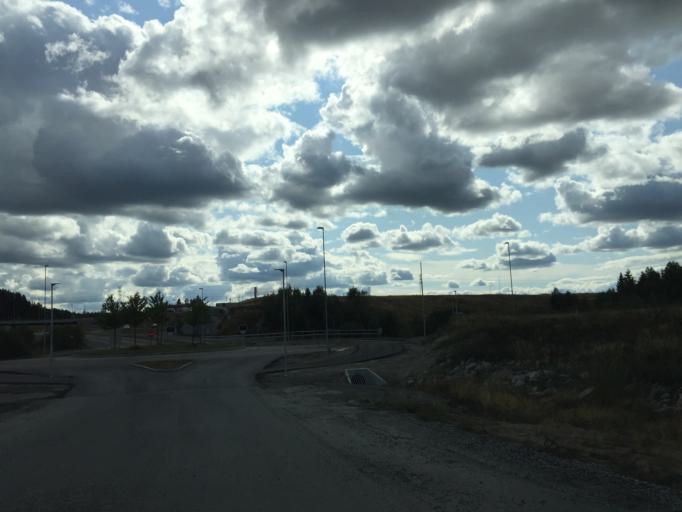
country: NO
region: Ostfold
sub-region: Hobol
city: Knappstad
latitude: 59.6217
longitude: 11.0060
